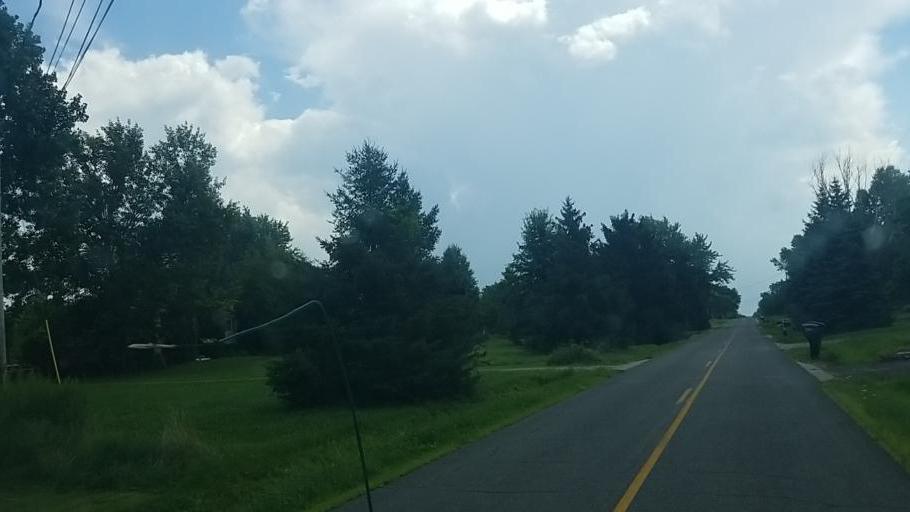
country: US
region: Ohio
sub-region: Lorain County
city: Grafton
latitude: 41.1618
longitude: -81.9941
